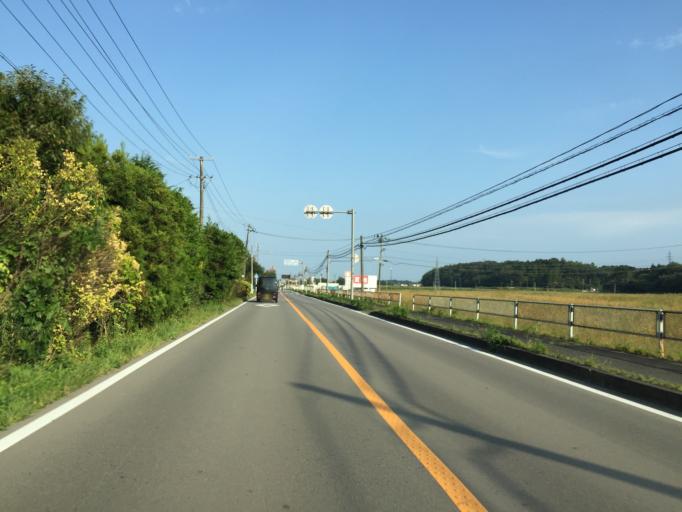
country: JP
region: Fukushima
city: Namie
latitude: 37.4990
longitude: 140.9587
